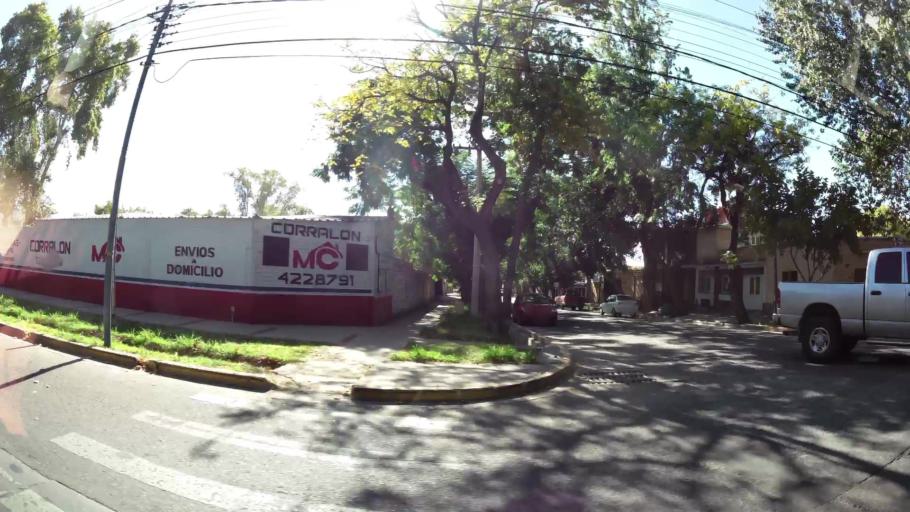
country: AR
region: Mendoza
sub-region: Departamento de Godoy Cruz
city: Godoy Cruz
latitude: -32.9350
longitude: -68.8588
